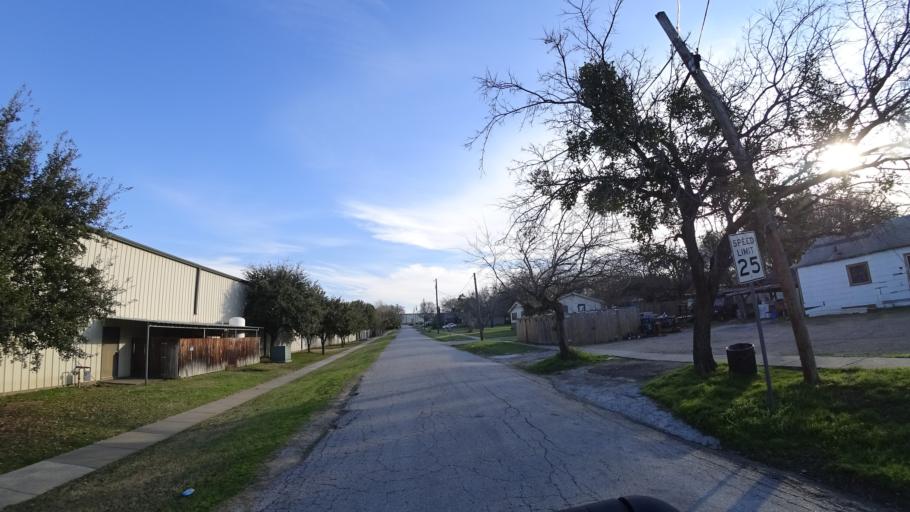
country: US
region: Texas
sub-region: Denton County
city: Lewisville
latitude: 33.0419
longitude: -96.9904
